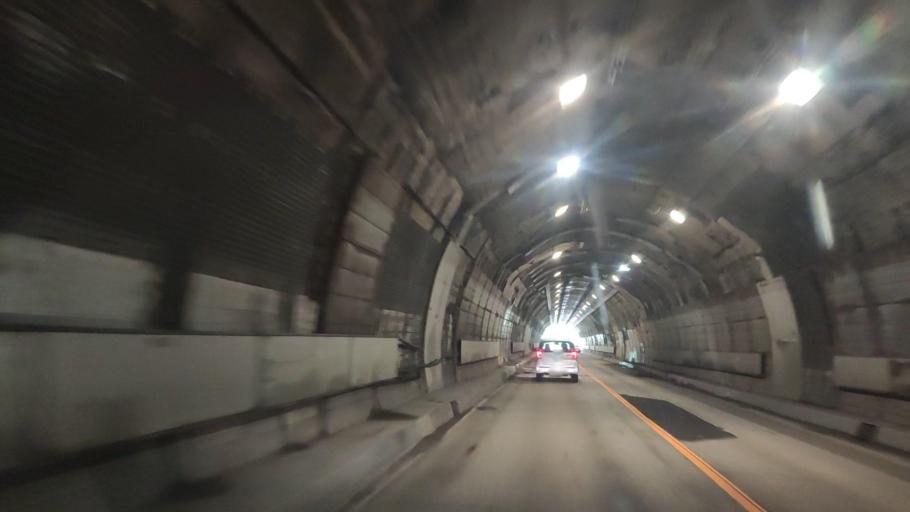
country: JP
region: Hokkaido
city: Date
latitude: 42.5712
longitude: 140.7332
